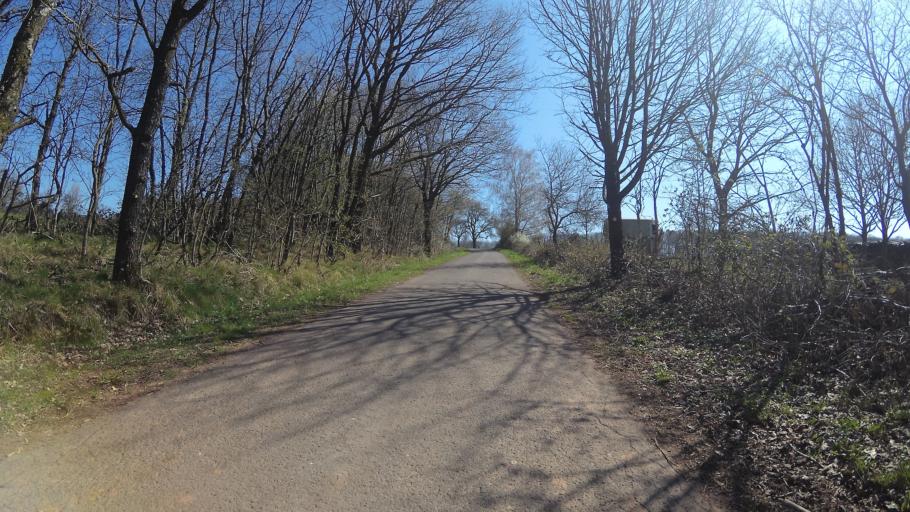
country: DE
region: Rheinland-Pfalz
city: Breitenbach
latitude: 49.4135
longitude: 7.2463
